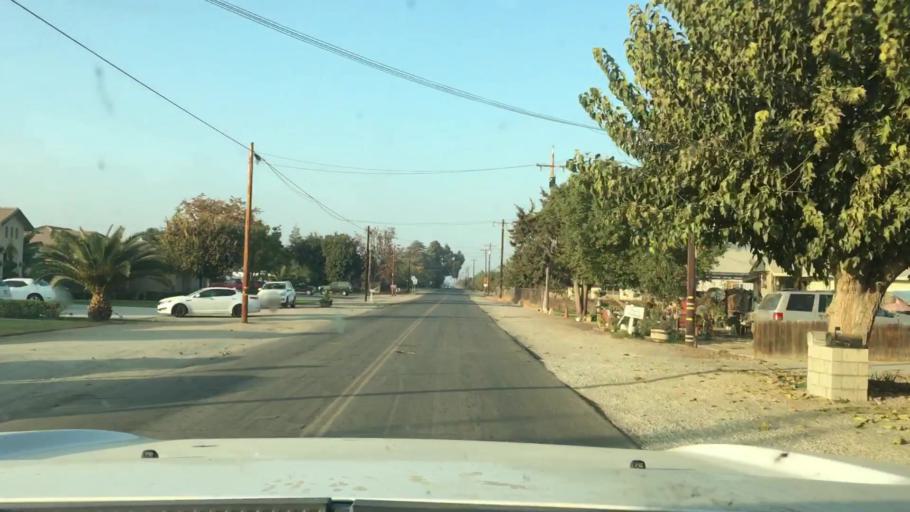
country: US
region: California
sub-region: Kern County
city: Shafter
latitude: 35.4837
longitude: -119.2963
